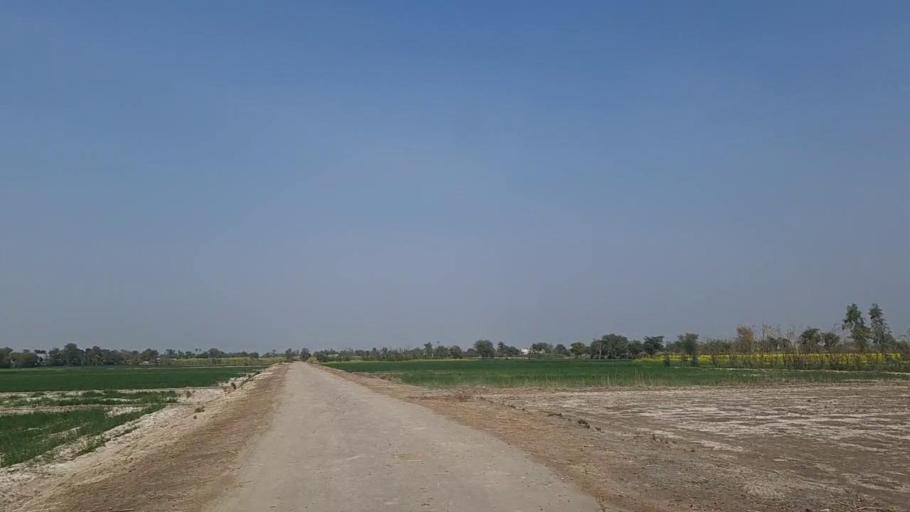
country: PK
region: Sindh
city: Daur
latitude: 26.4895
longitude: 68.4477
